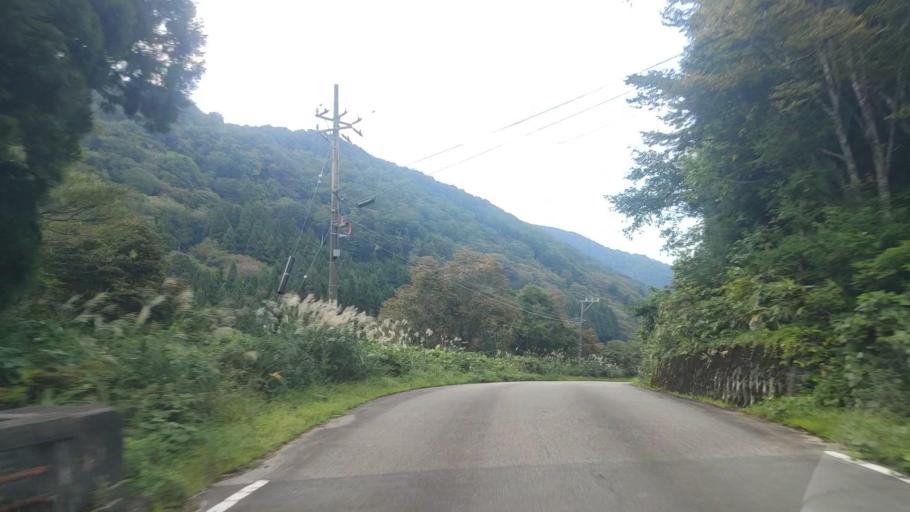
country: JP
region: Toyama
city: Yatsuomachi-higashikumisaka
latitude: 36.4271
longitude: 137.0820
